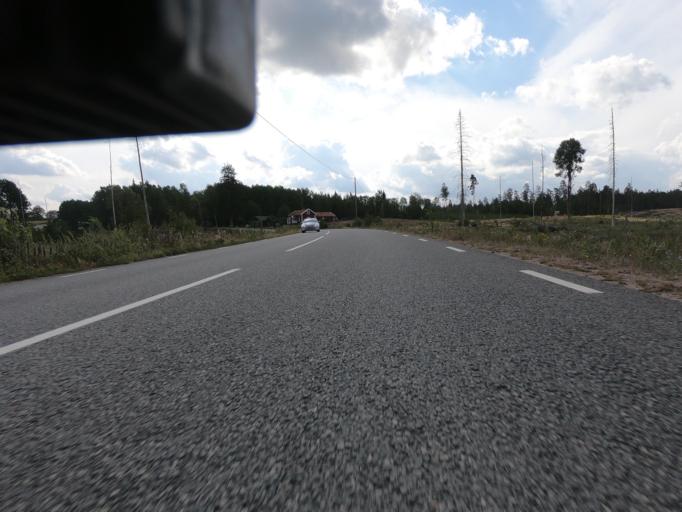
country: SE
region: Joenkoeping
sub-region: Vetlanda Kommun
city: Landsbro
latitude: 57.2963
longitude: 14.8729
